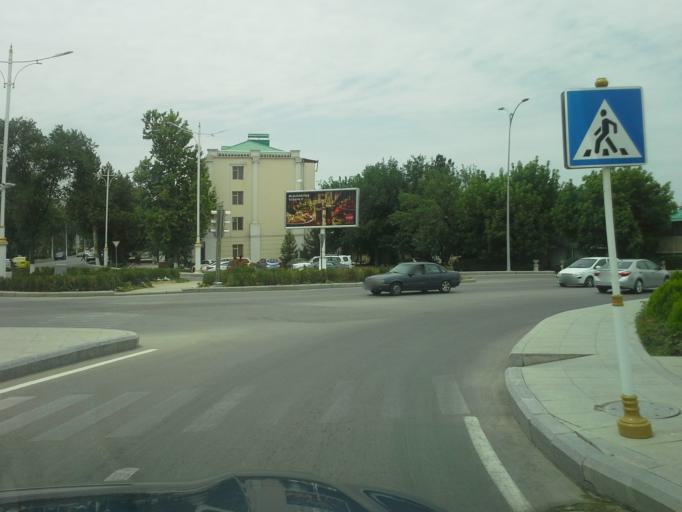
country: TM
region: Ahal
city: Ashgabat
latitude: 37.9433
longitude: 58.3606
